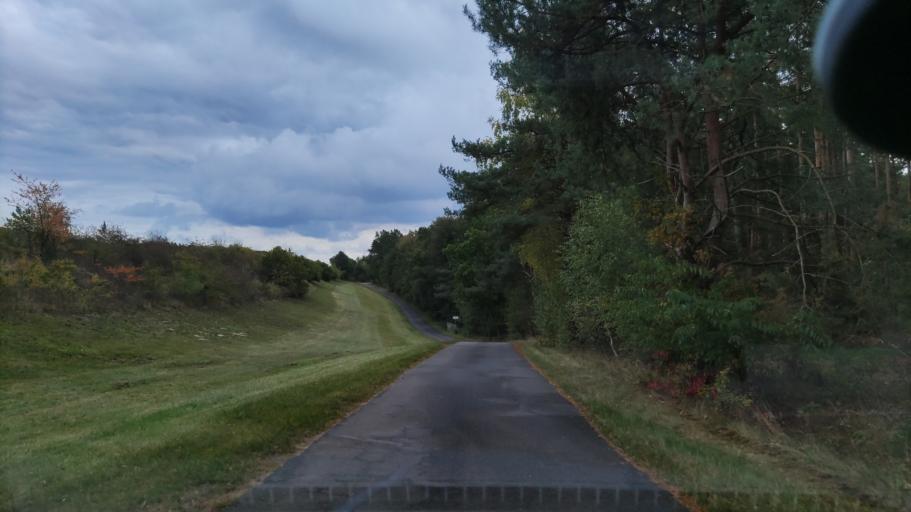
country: DE
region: Lower Saxony
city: Vastorf
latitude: 53.1667
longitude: 10.5283
